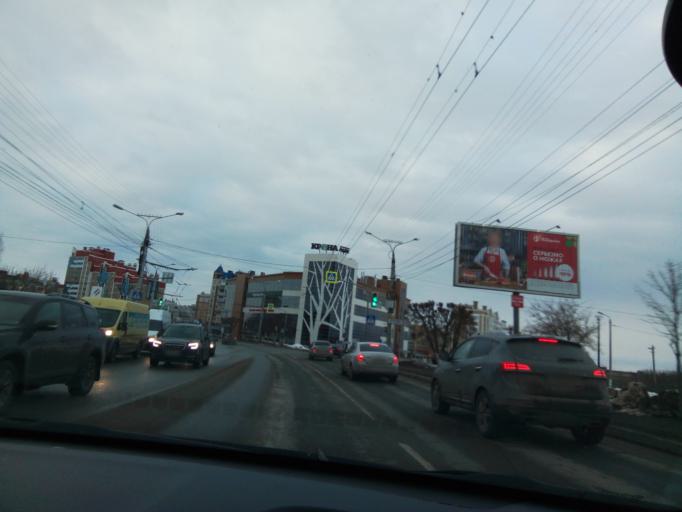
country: RU
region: Chuvashia
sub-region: Cheboksarskiy Rayon
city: Cheboksary
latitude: 56.1477
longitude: 47.2019
